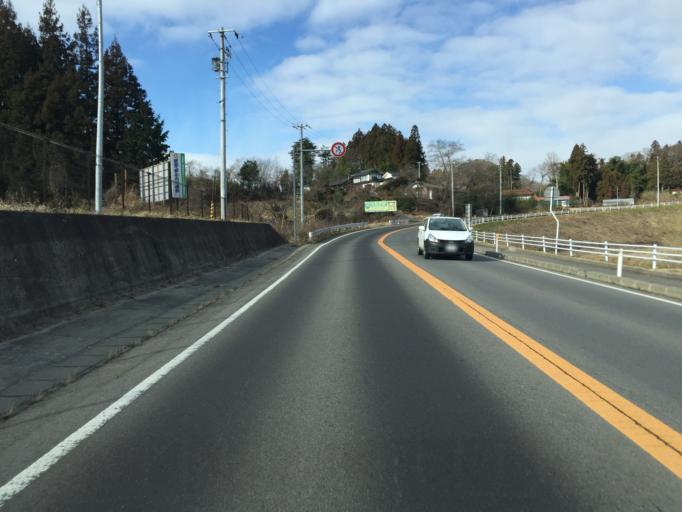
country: JP
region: Fukushima
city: Fukushima-shi
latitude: 37.6821
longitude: 140.5501
